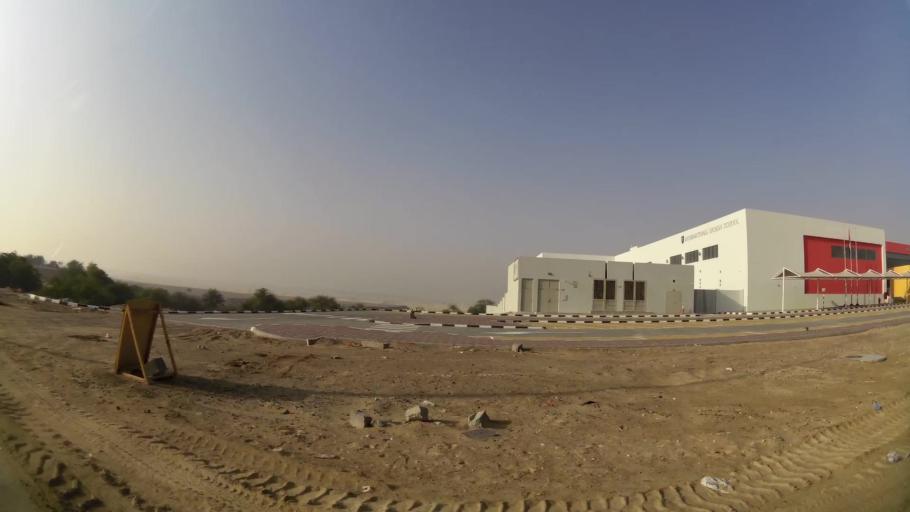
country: AE
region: Abu Dhabi
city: Abu Dhabi
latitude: 24.2949
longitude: 54.6199
